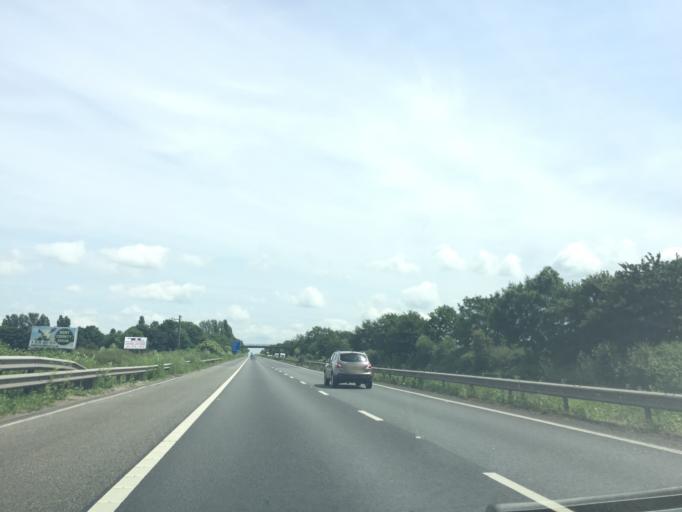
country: GB
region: England
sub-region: Kent
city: Newington
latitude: 51.3380
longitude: 0.6409
